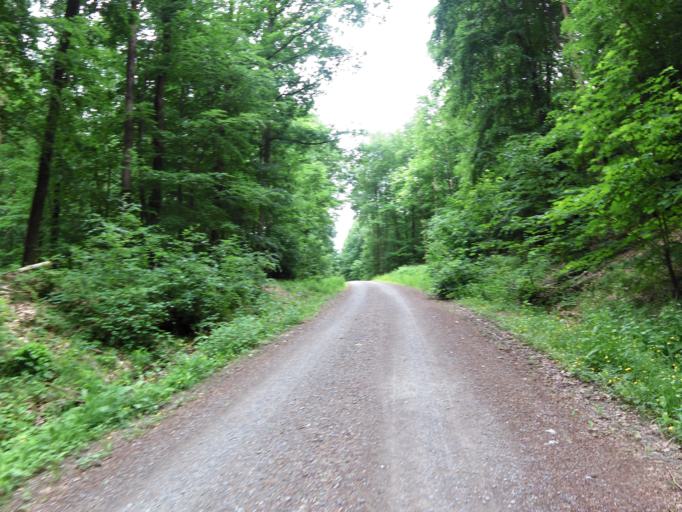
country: DE
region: Bavaria
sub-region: Regierungsbezirk Unterfranken
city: Kleinrinderfeld
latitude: 49.7135
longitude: 9.8179
